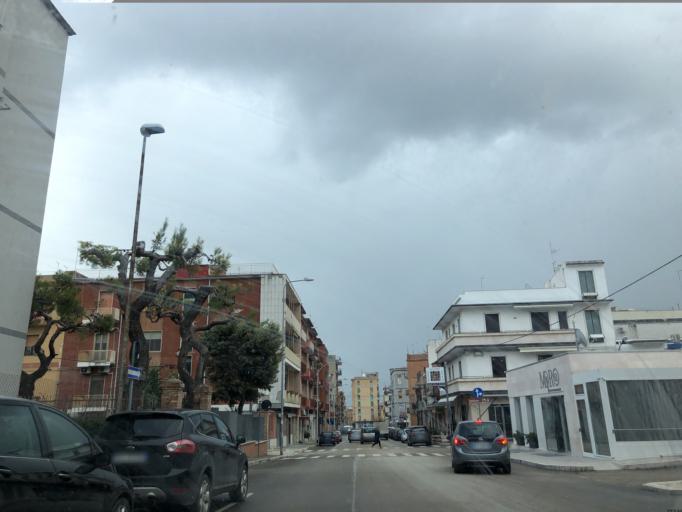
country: IT
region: Apulia
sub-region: Provincia di Foggia
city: Lucera
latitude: 41.5117
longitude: 15.3357
